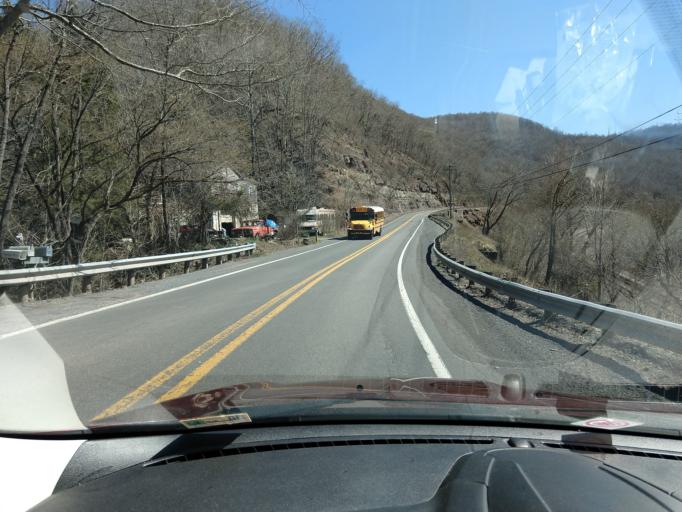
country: US
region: West Virginia
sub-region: Summers County
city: Hinton
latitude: 37.6939
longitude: -80.8771
